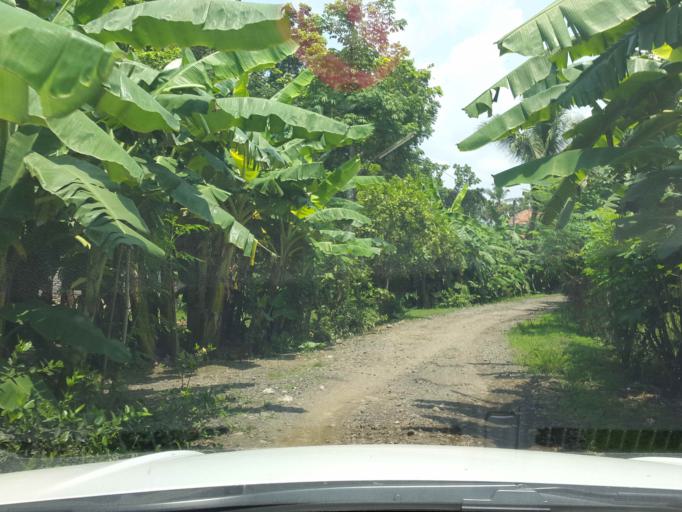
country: ID
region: Central Java
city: Winangun
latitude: -7.3597
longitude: 108.6935
